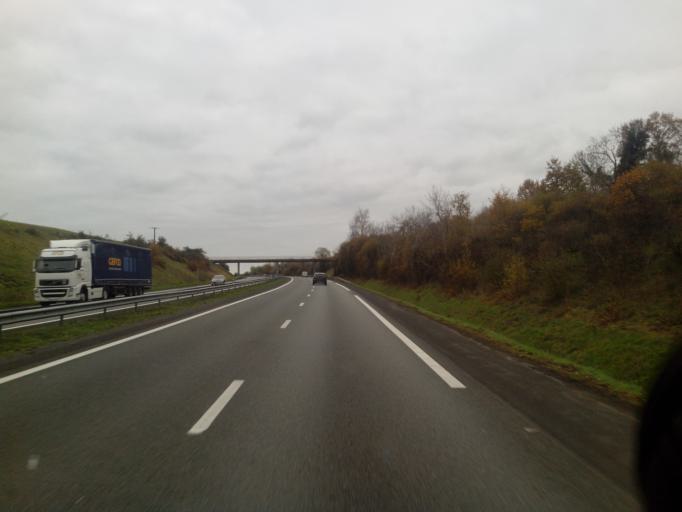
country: FR
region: Pays de la Loire
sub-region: Departement de Maine-et-Loire
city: Tillieres
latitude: 47.1485
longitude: -1.1939
